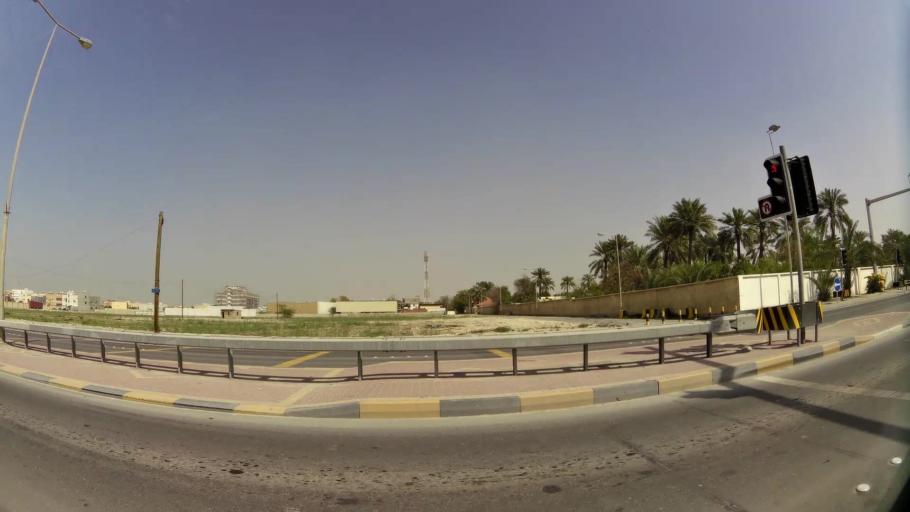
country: BH
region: Manama
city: Jidd Hafs
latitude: 26.2034
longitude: 50.4589
